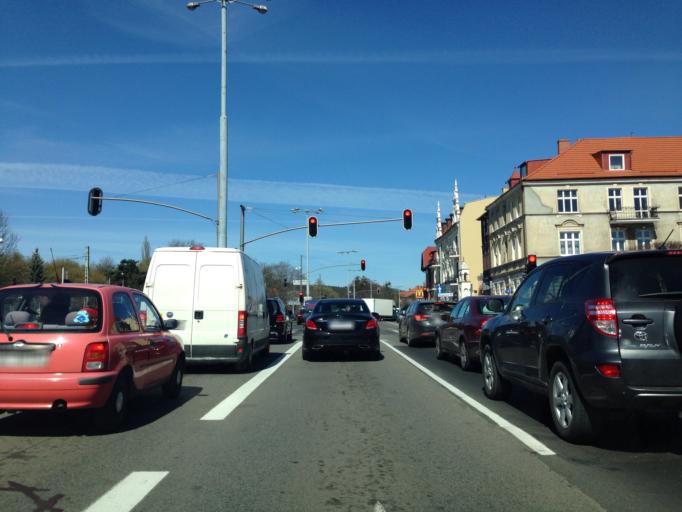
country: PL
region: Pomeranian Voivodeship
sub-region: Sopot
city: Sopot
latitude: 54.4097
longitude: 18.5679
